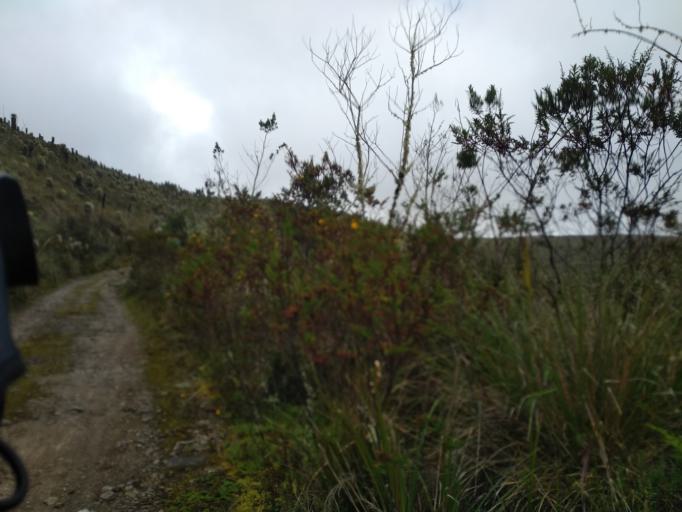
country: EC
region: Carchi
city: San Gabriel
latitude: 0.6925
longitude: -77.8493
